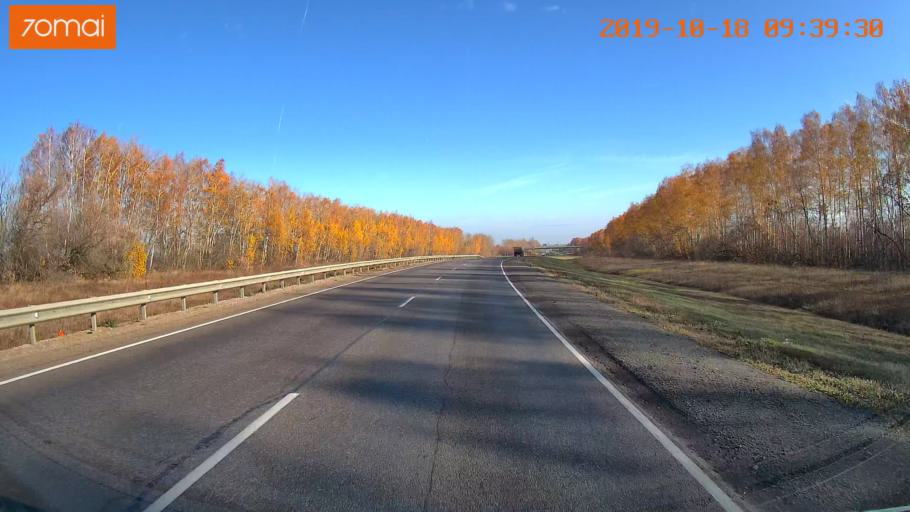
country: RU
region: Tula
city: Yefremov
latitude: 53.2539
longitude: 38.1360
